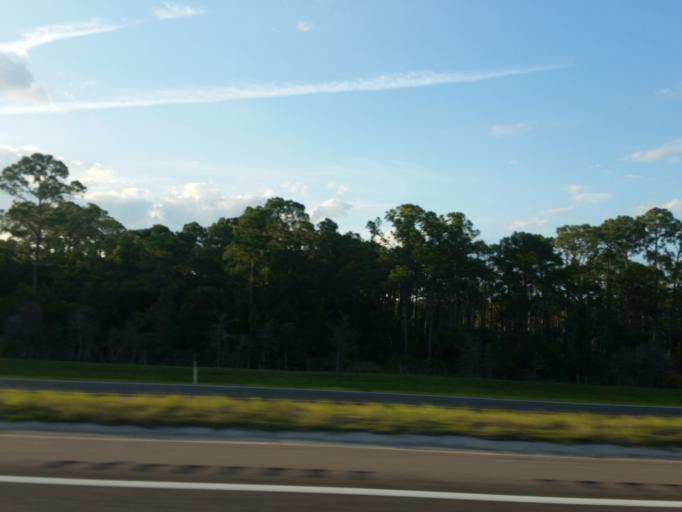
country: US
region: Florida
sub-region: Sarasota County
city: Plantation
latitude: 27.1100
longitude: -82.3514
